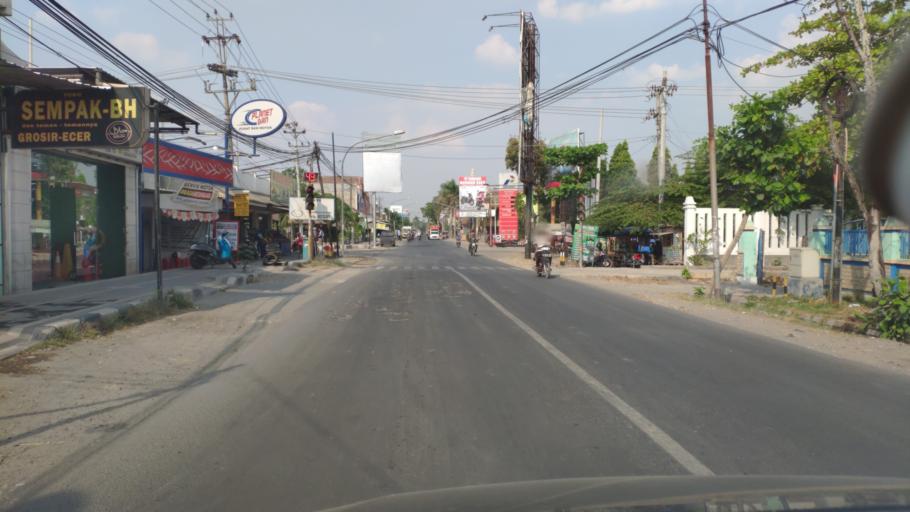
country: ID
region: Central Java
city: Tambakkromo
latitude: -7.1543
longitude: 111.5808
